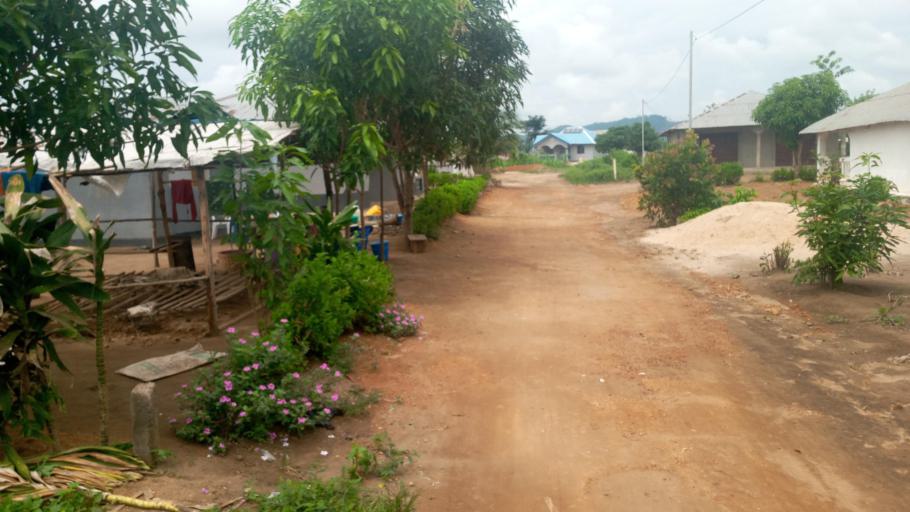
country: SL
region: Southern Province
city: Mogbwemo
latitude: 7.7759
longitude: -12.3029
